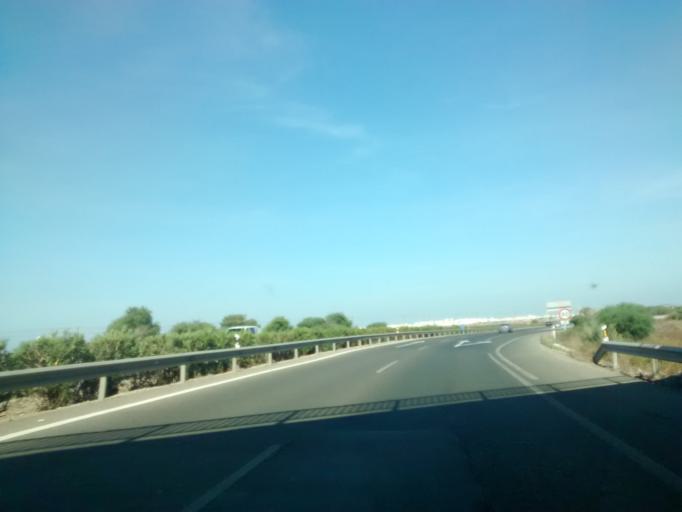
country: ES
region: Andalusia
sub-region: Provincia de Cadiz
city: Chiclana de la Frontera
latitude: 36.4450
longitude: -6.1452
